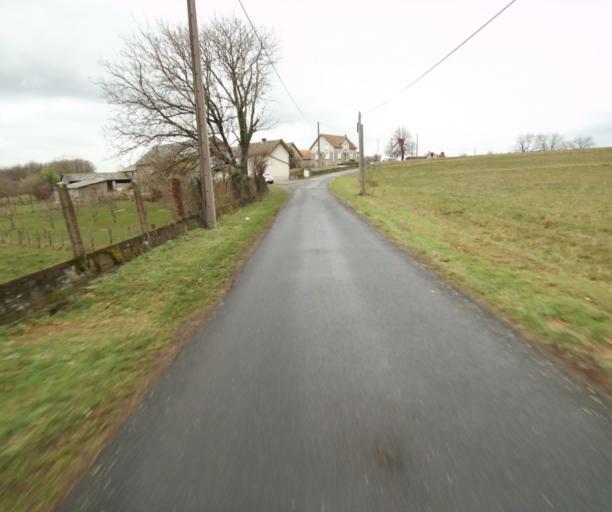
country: FR
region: Limousin
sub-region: Departement de la Correze
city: Saint-Mexant
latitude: 45.2801
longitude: 1.6331
